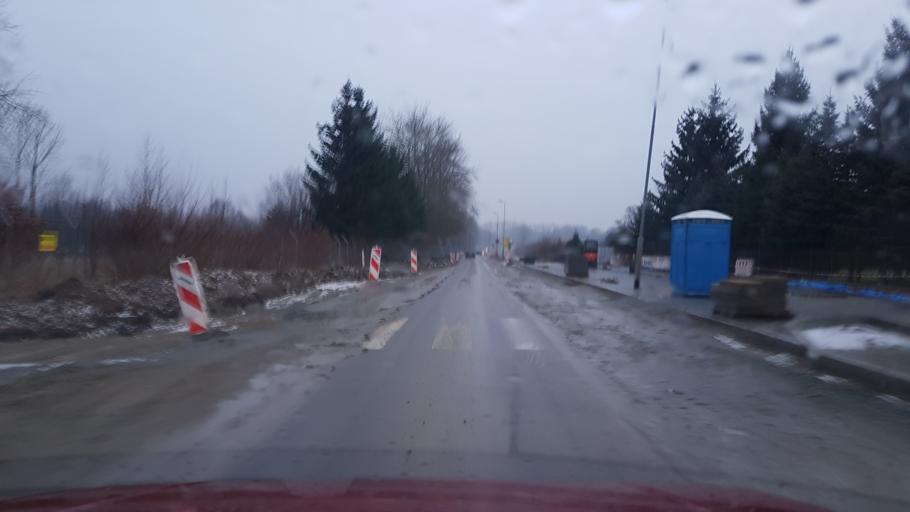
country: PL
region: West Pomeranian Voivodeship
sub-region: Koszalin
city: Koszalin
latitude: 54.1800
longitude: 16.2196
